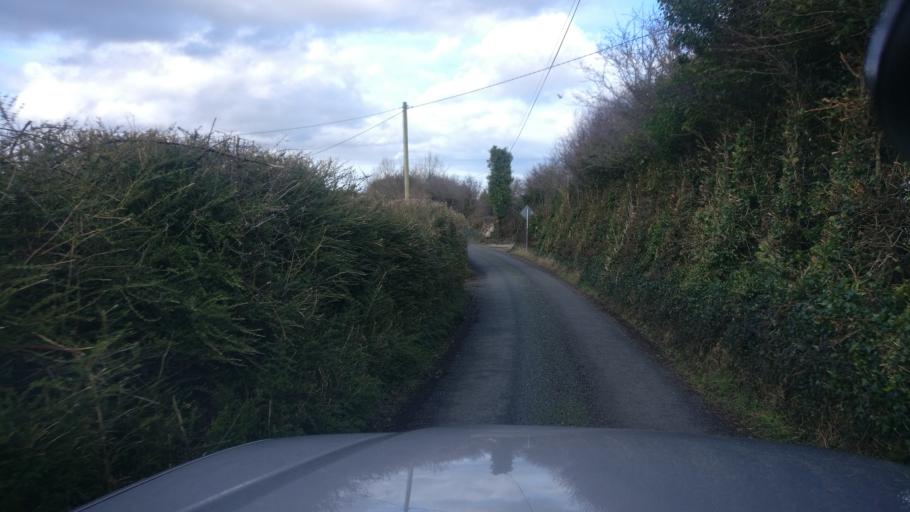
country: IE
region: Connaught
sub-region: County Galway
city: Loughrea
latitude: 53.2026
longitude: -8.4310
